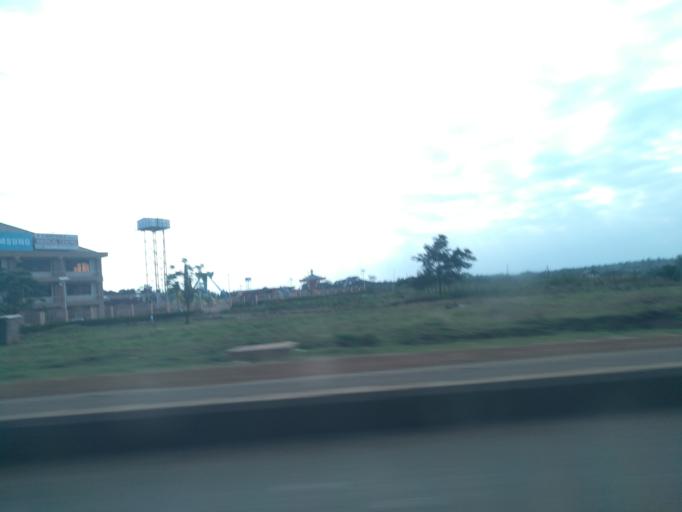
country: KE
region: Nairobi Area
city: Thika
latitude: -1.1171
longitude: 37.0104
